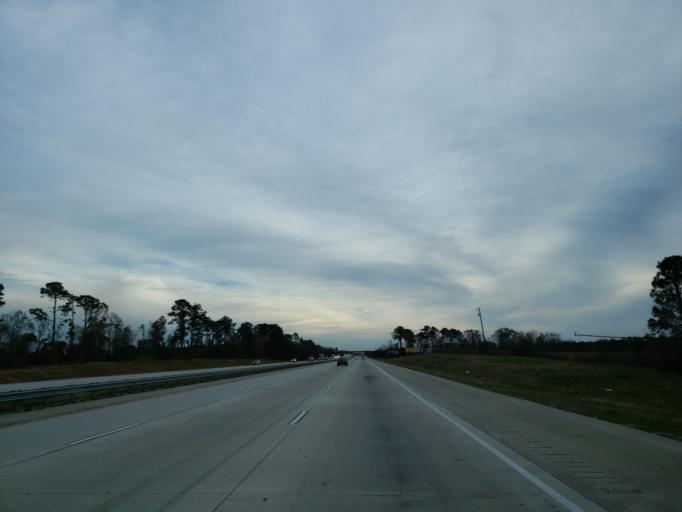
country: US
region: Georgia
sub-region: Dooly County
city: Vienna
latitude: 32.0737
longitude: -83.7618
